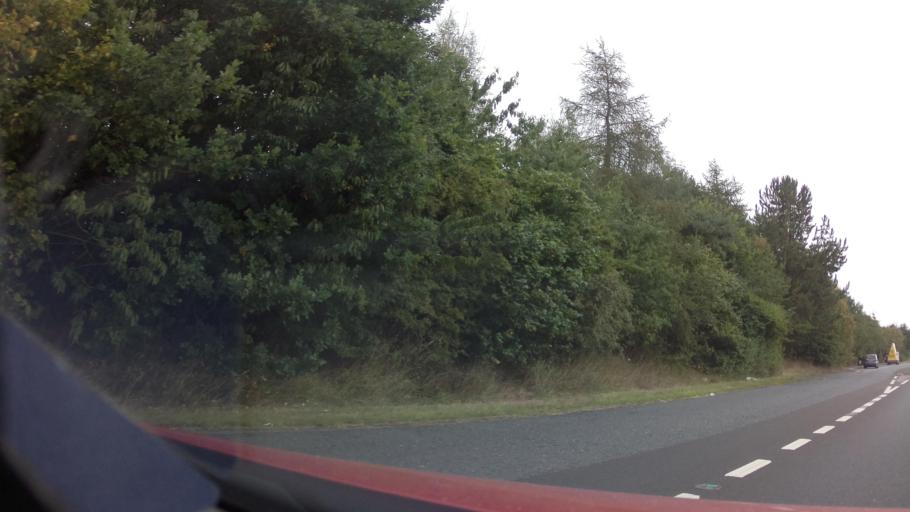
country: GB
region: England
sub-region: Newcastle upon Tyne
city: Dinnington
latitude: 55.0214
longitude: -1.6989
